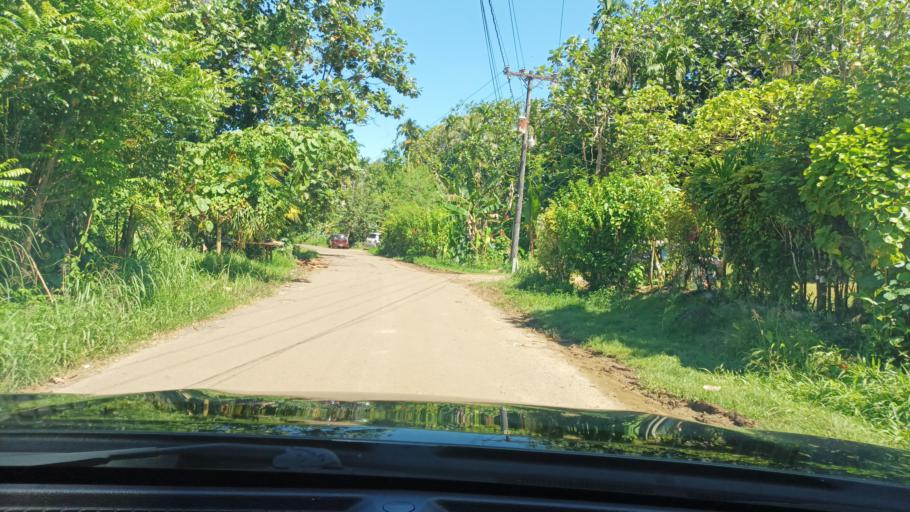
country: FM
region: Pohnpei
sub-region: Madolenihm Municipality
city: Madolenihm Municipality Government
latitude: 6.8437
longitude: 158.3052
